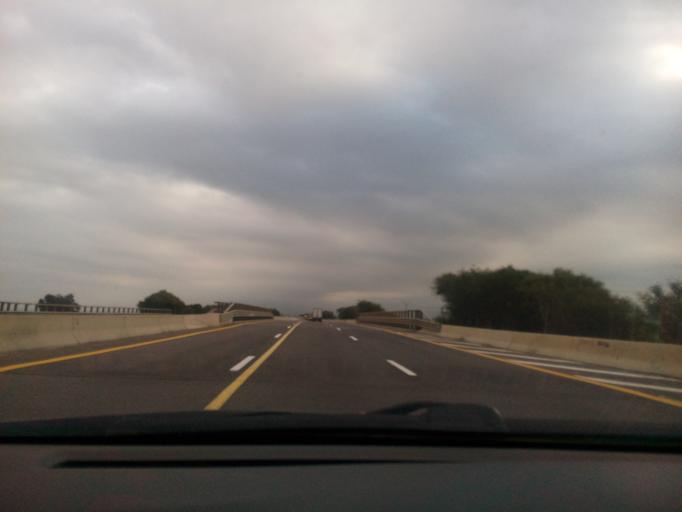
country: DZ
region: Relizane
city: Relizane
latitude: 35.7912
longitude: 0.4580
